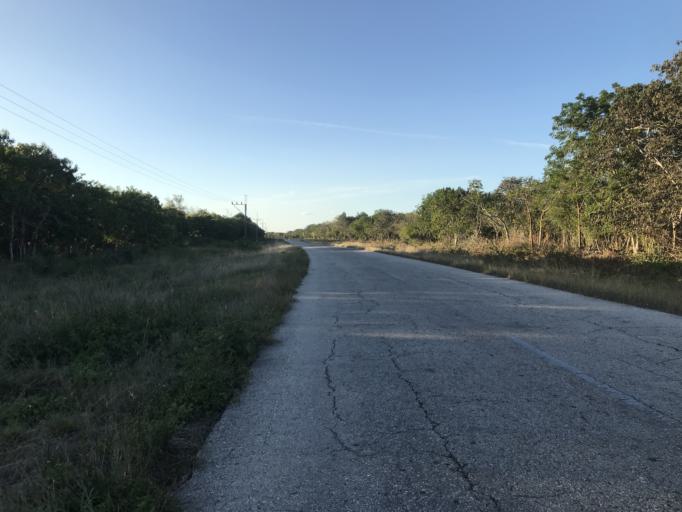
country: CU
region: Cienfuegos
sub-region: Municipio de Aguada de Pasajeros
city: Aguada de Pasajeros
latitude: 22.0730
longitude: -81.0567
